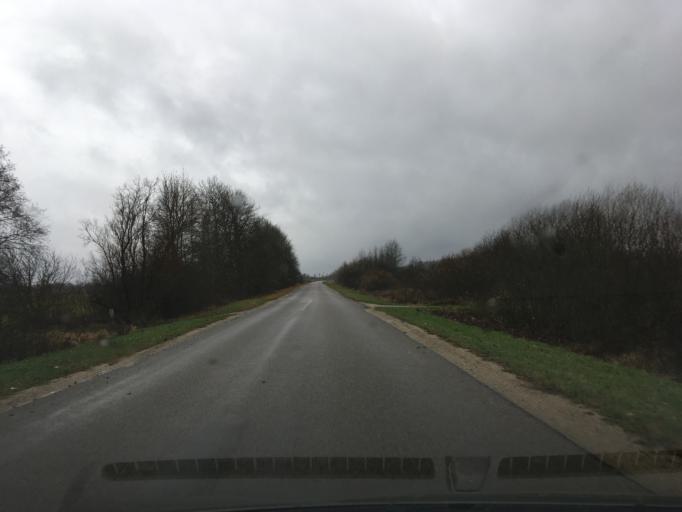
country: EE
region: Laeaene
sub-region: Lihula vald
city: Lihula
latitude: 58.6993
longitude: 23.8552
